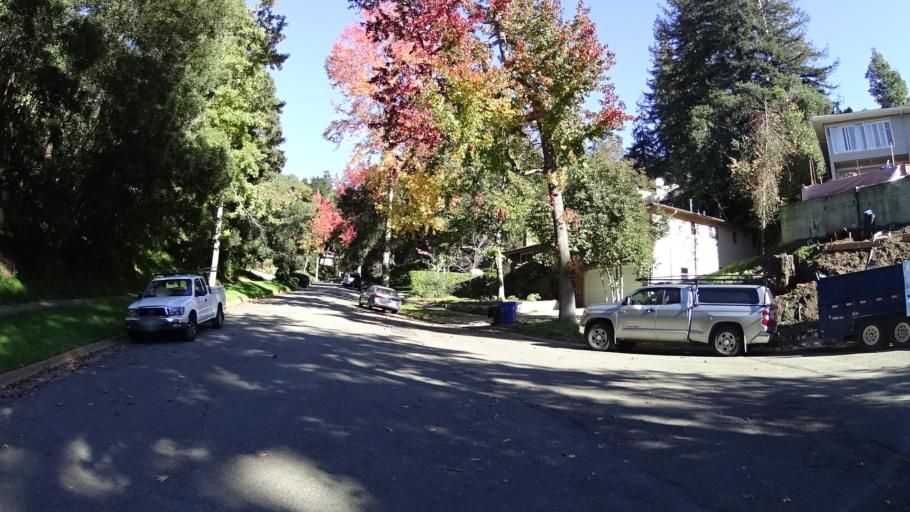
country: US
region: California
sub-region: Alameda County
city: Piedmont
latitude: 37.8200
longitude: -122.2164
